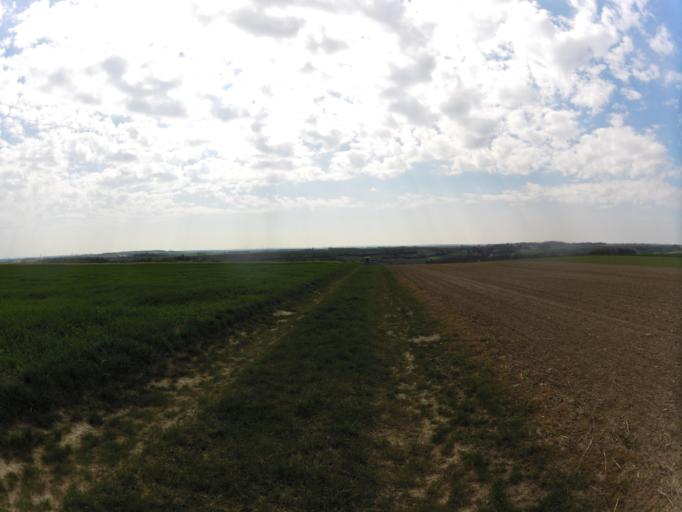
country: DE
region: Bavaria
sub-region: Regierungsbezirk Unterfranken
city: Winterhausen
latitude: 49.6808
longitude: 10.0064
